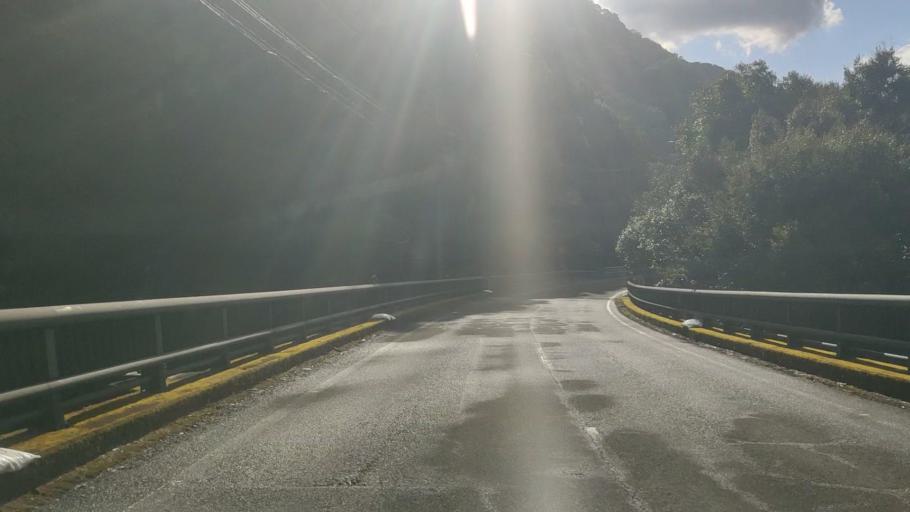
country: JP
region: Kumamoto
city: Hitoyoshi
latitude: 32.3793
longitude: 130.8378
